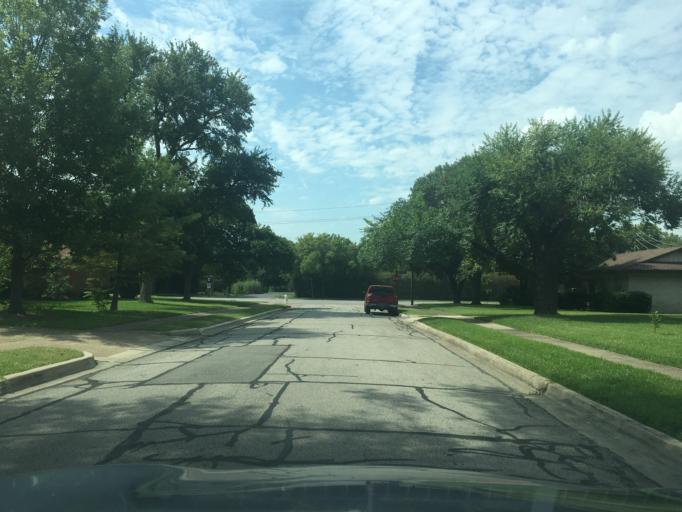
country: US
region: Texas
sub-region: Dallas County
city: Farmers Branch
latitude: 32.9257
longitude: -96.8693
